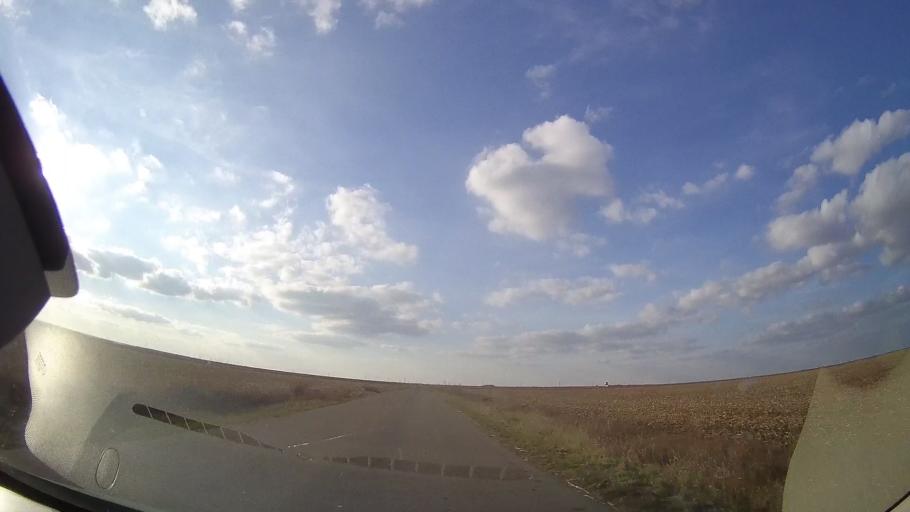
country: RO
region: Constanta
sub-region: Comuna Cerchezu
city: Cerchezu
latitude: 43.8251
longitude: 28.1339
